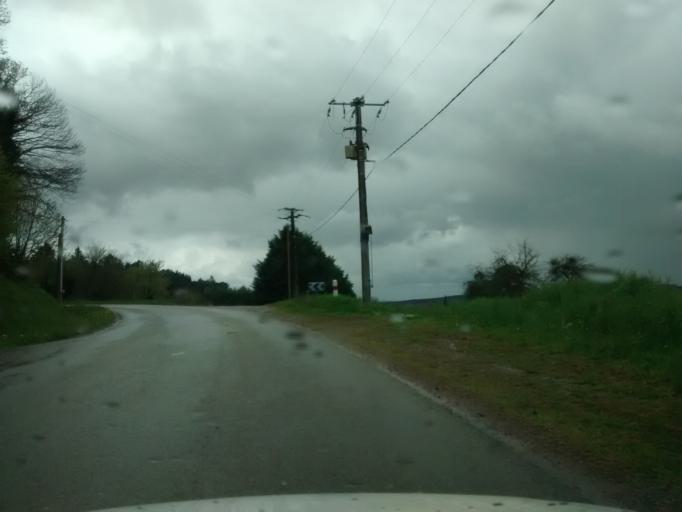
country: FR
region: Brittany
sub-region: Departement du Morbihan
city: Pleucadeuc
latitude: 47.7612
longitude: -2.3542
